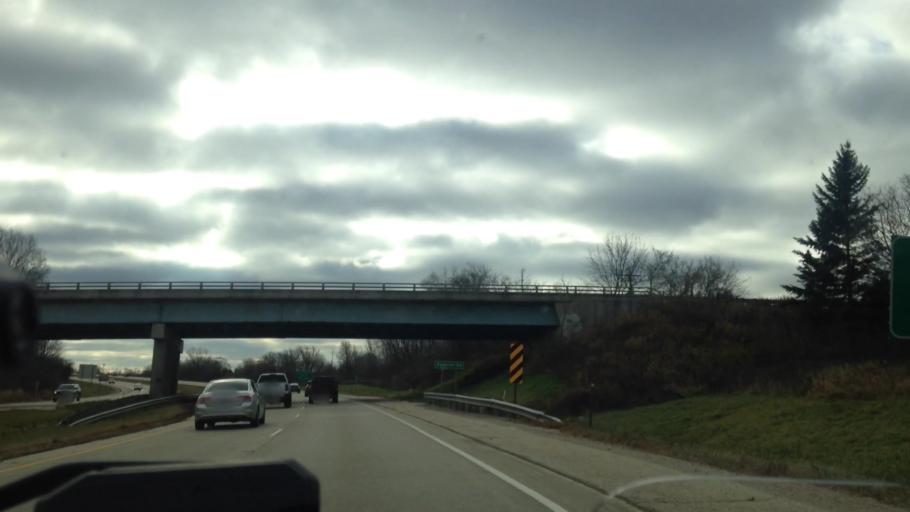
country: US
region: Wisconsin
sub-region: Washington County
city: West Bend
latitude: 43.4133
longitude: -88.2063
